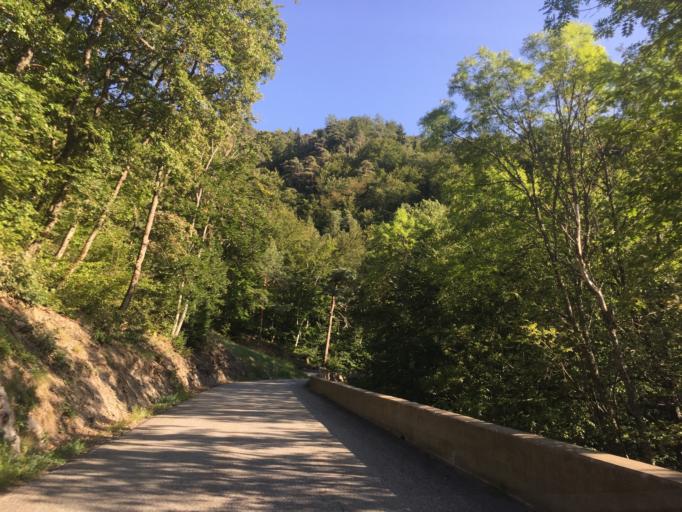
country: FR
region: Rhone-Alpes
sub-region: Departement de la Savoie
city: Moutiers
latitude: 45.5042
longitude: 6.5747
